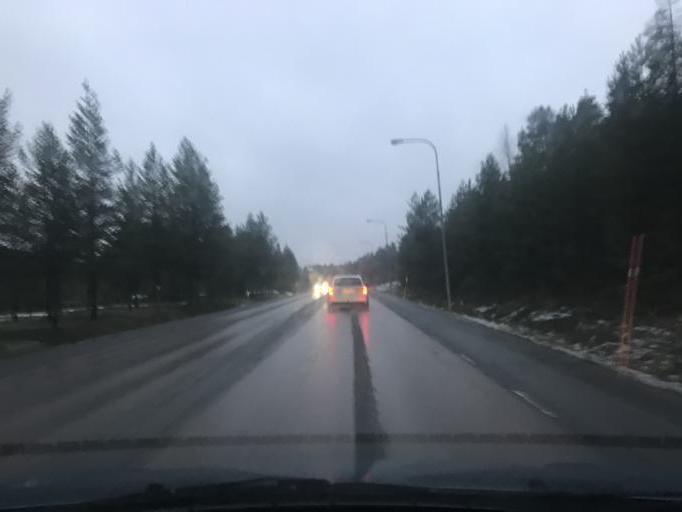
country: SE
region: Norrbotten
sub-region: Lulea Kommun
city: Gammelstad
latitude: 65.6238
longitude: 22.0357
